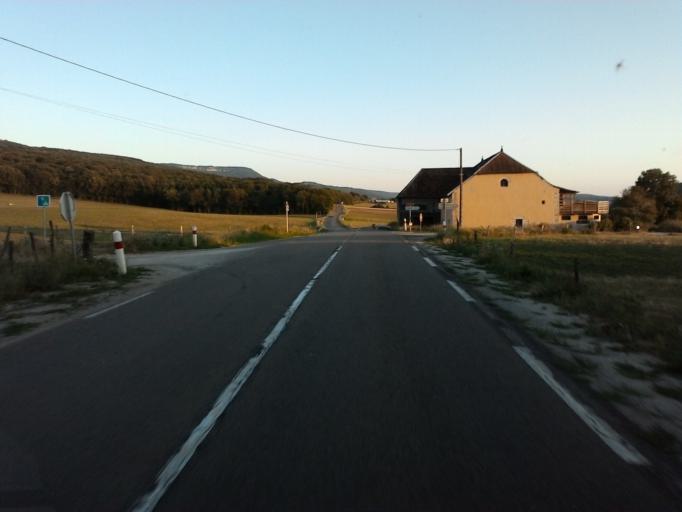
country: FR
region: Franche-Comte
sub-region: Departement du Doubs
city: Quingey
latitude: 47.0400
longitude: 5.8744
